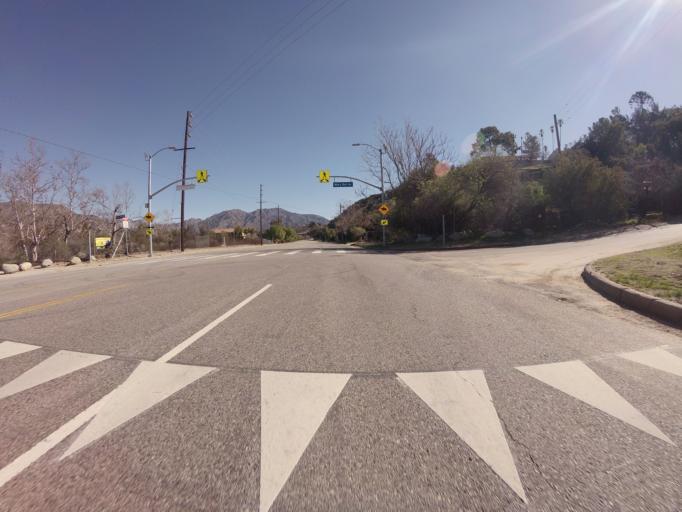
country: US
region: California
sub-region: Los Angeles County
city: Burbank
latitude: 34.2642
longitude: -118.3443
